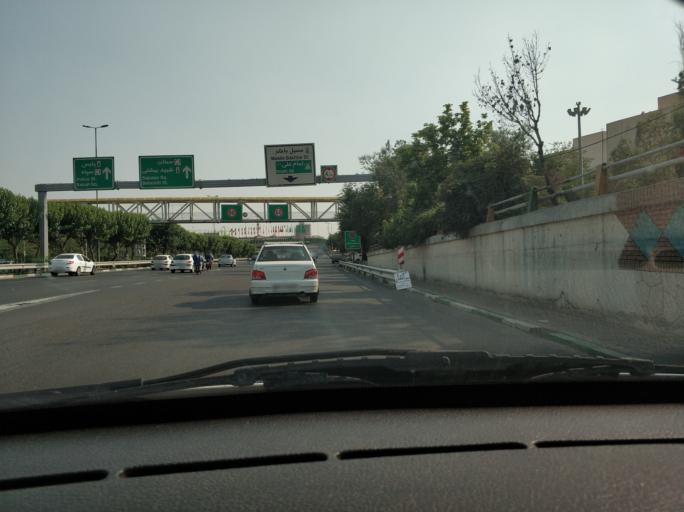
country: IR
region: Tehran
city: Tehran
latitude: 35.7387
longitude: 51.4590
